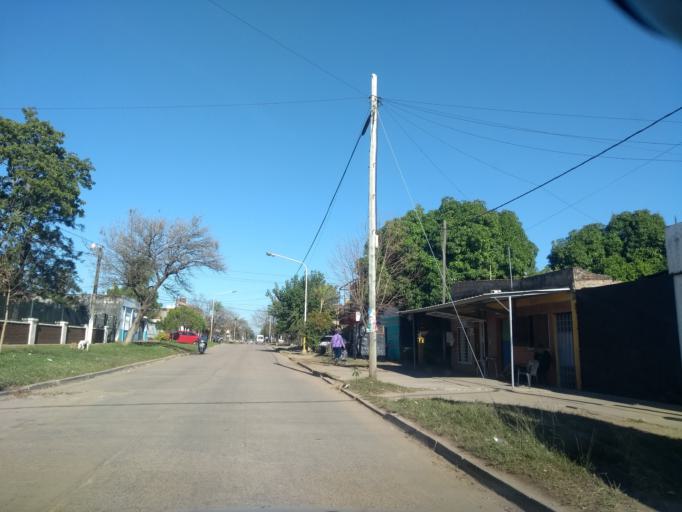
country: AR
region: Chaco
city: Barranqueras
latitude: -27.4828
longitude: -58.9273
